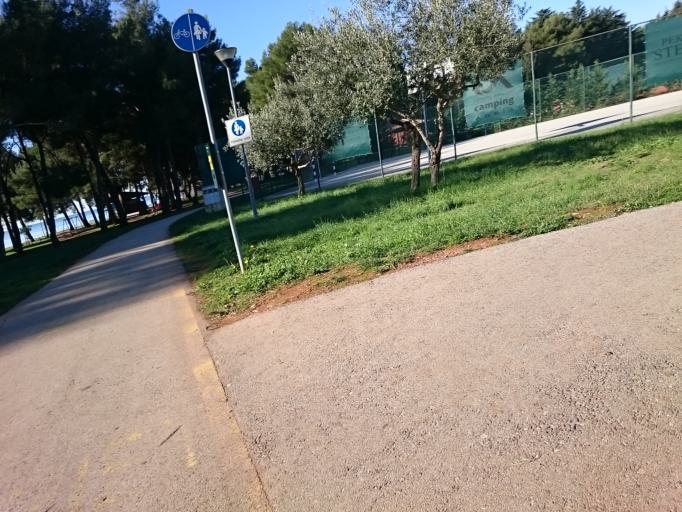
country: HR
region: Istarska
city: Novigrad
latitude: 45.3237
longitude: 13.5612
